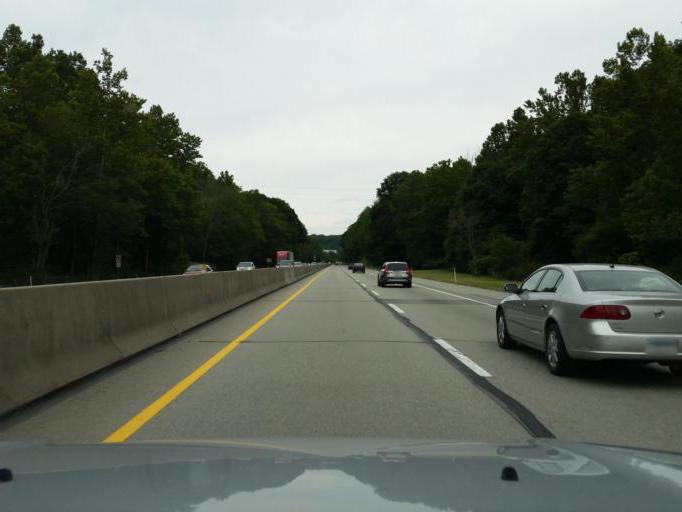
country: US
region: Pennsylvania
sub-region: Westmoreland County
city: Level Green
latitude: 40.4027
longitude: -79.7060
